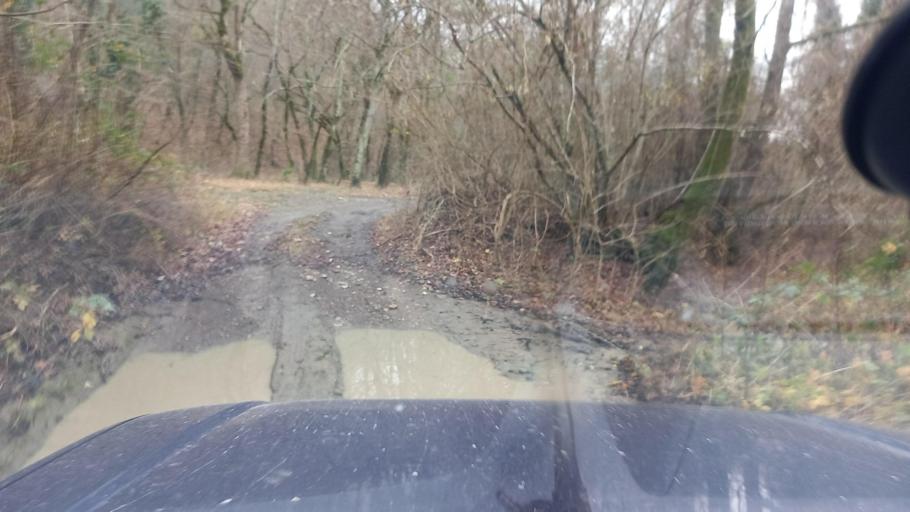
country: RU
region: Krasnodarskiy
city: Pshada
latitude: 44.4897
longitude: 38.4158
